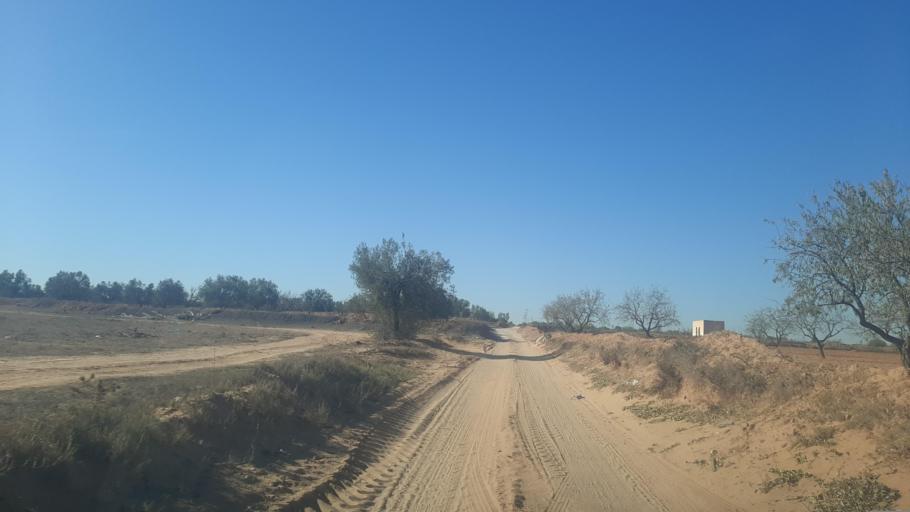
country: TN
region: Safaqis
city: Sfax
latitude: 34.8946
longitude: 10.5961
